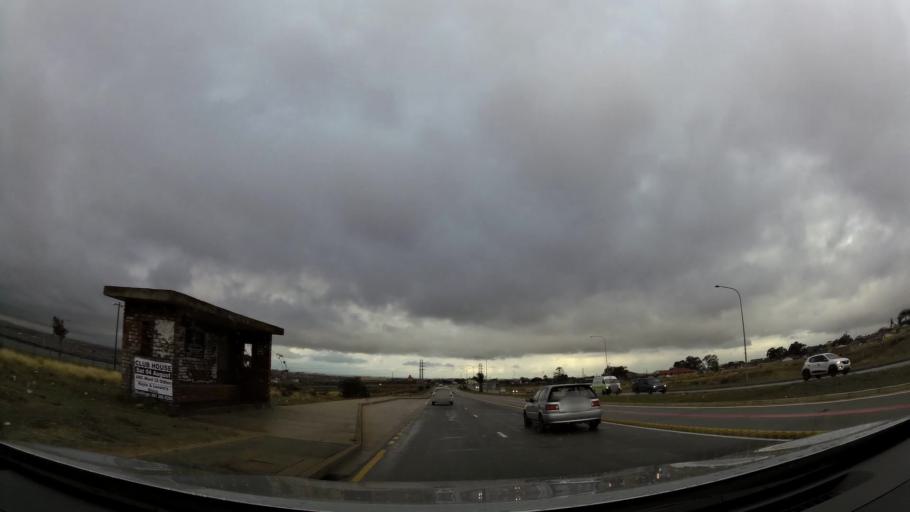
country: ZA
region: Eastern Cape
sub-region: Nelson Mandela Bay Metropolitan Municipality
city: Port Elizabeth
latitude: -33.8960
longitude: 25.5356
